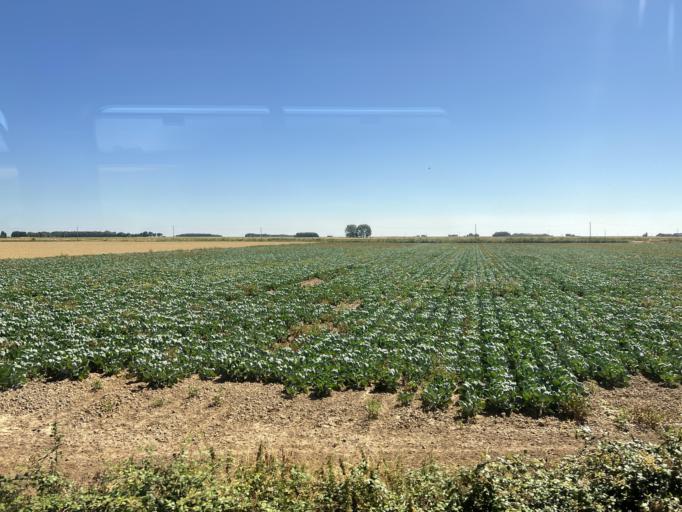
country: GB
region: England
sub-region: Lincolnshire
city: Wainfleet All Saints
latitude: 53.1079
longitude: 0.2533
